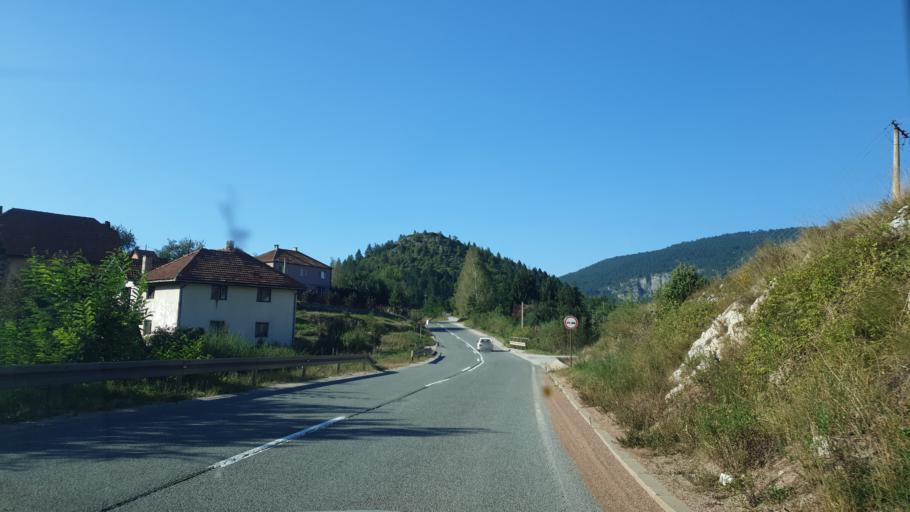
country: RS
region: Central Serbia
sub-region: Zlatiborski Okrug
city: Nova Varos
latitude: 43.5429
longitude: 19.7876
